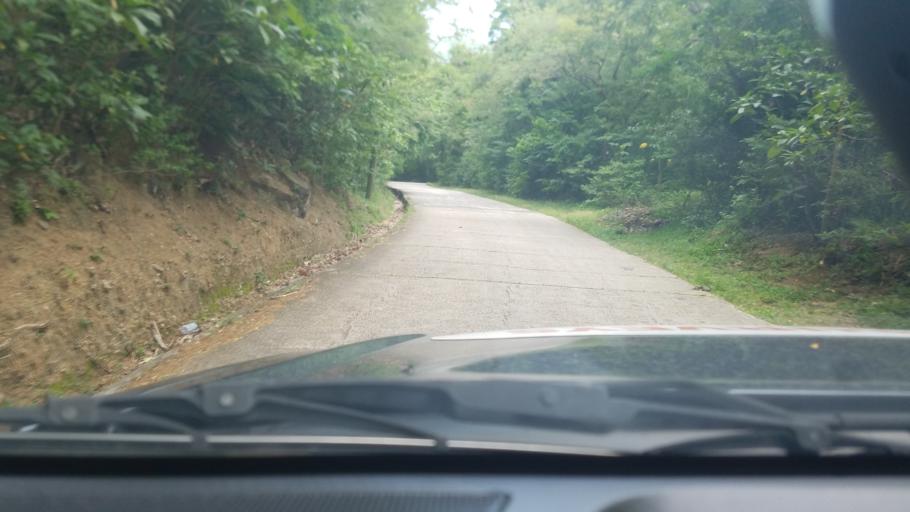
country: LC
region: Soufriere
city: Soufriere
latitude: 13.8352
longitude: -61.0592
